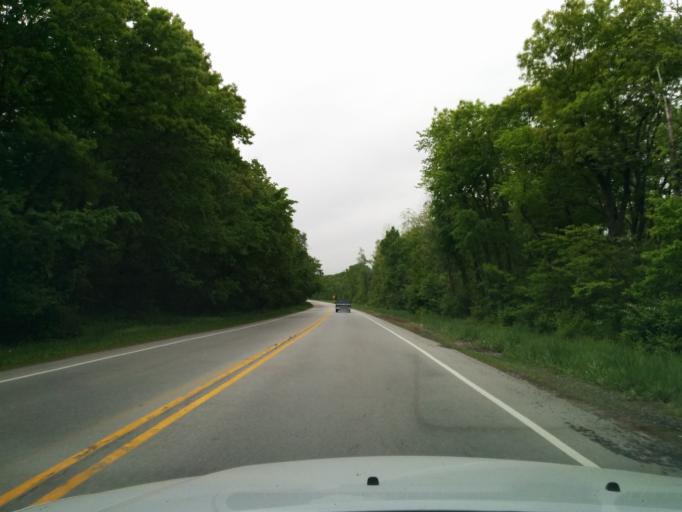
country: US
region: Illinois
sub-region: Cook County
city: Palos Park
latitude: 41.6830
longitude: -87.8378
